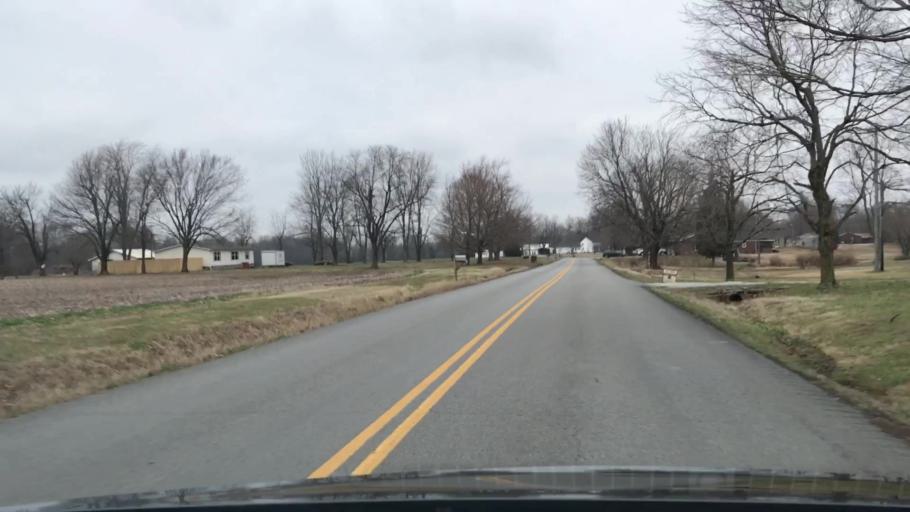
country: US
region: Kentucky
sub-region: Muhlenberg County
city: Morehead
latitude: 37.3370
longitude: -87.2210
